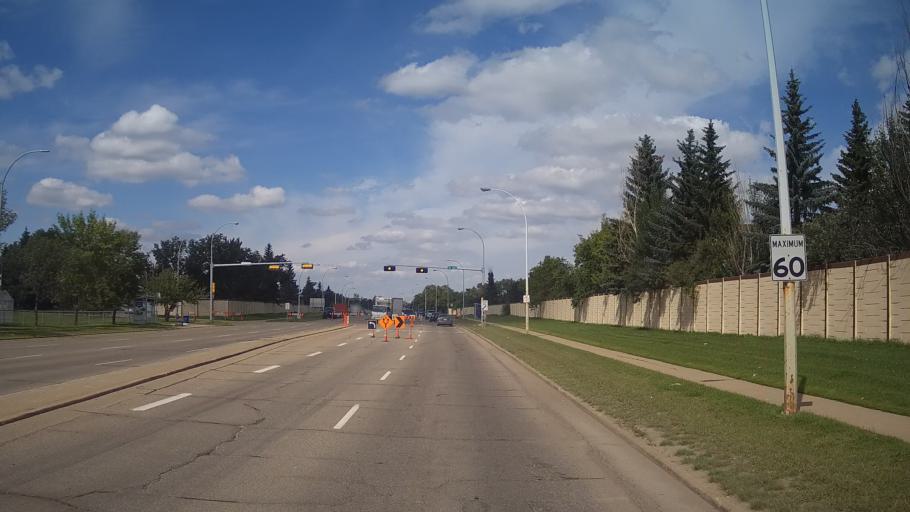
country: CA
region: Alberta
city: St. Albert
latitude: 53.5255
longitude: -113.6299
